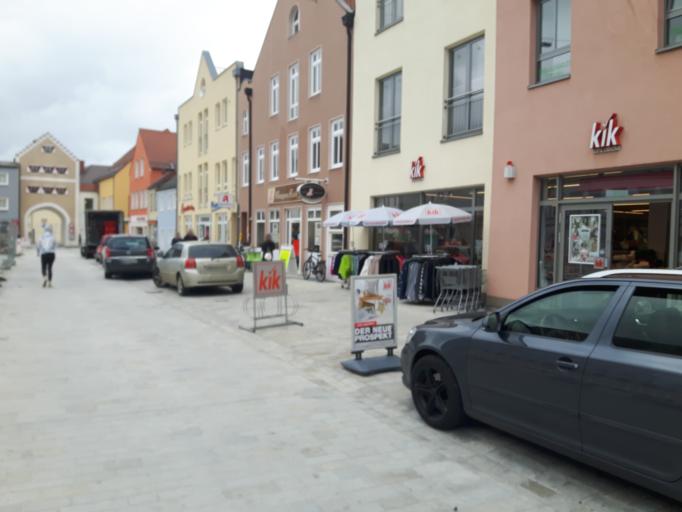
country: DE
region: Bavaria
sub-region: Lower Bavaria
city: Dingolfing
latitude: 48.6295
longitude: 12.4990
